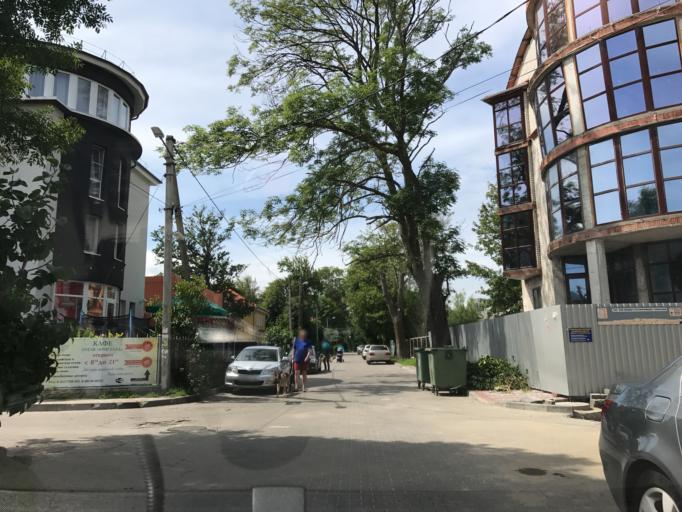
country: RU
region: Kaliningrad
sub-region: Zelenogradskiy Rayon
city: Zelenogradsk
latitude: 54.9582
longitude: 20.4651
